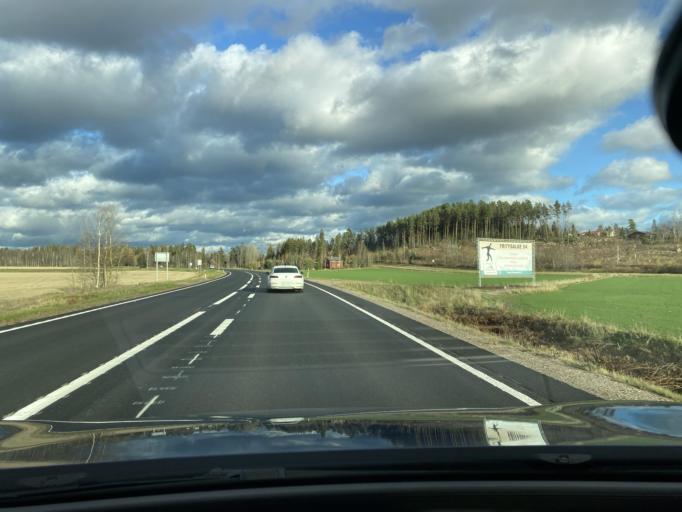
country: FI
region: Haeme
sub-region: Riihimaeki
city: Oitti
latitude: 60.7973
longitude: 25.0272
